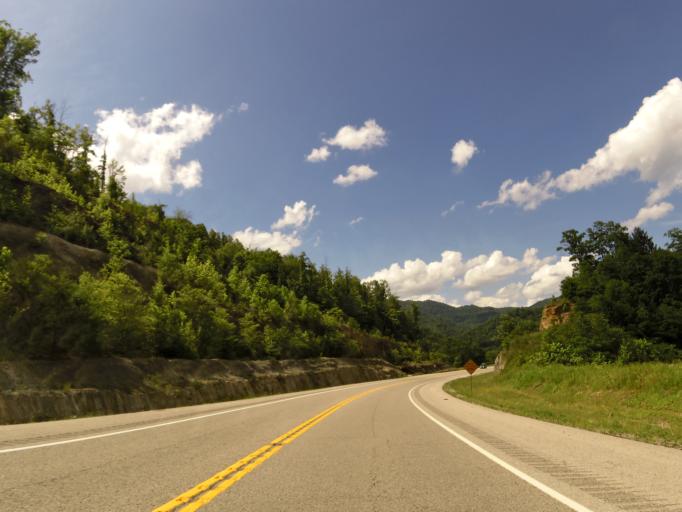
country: US
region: Kentucky
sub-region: Harlan County
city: Harlan
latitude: 36.8022
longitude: -83.2709
